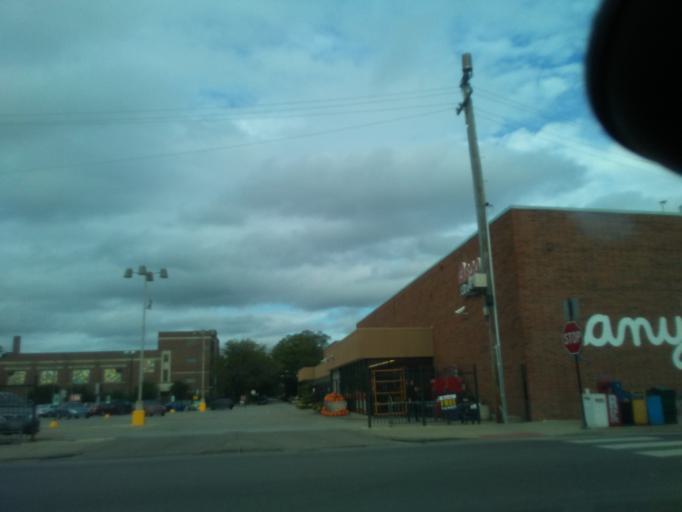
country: US
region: Illinois
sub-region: Cook County
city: Evanston
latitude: 41.9826
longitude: -87.6685
